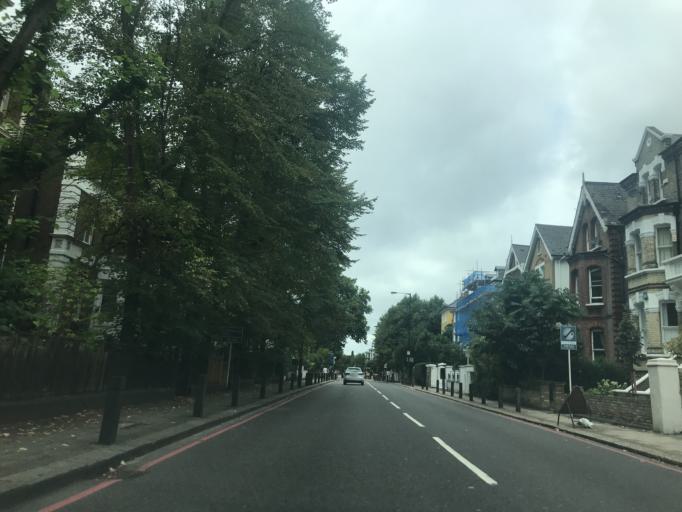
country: GB
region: England
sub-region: Greater London
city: Earlsfield
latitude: 51.4584
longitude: -0.1768
